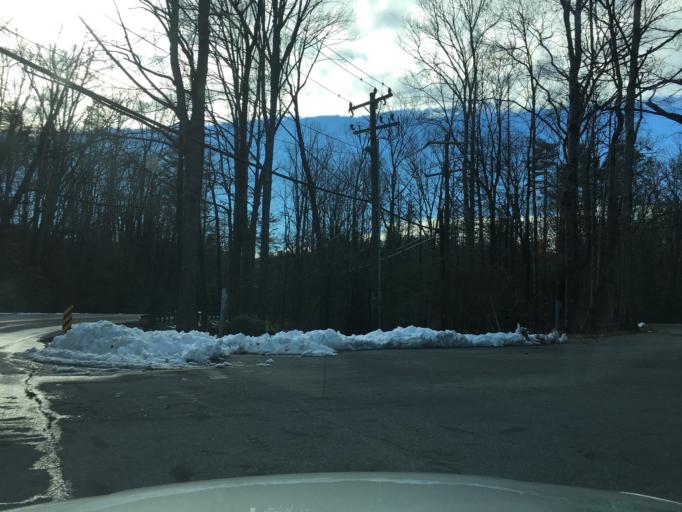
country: US
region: North Carolina
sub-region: Jackson County
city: Cullowhee
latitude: 35.1182
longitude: -83.0106
